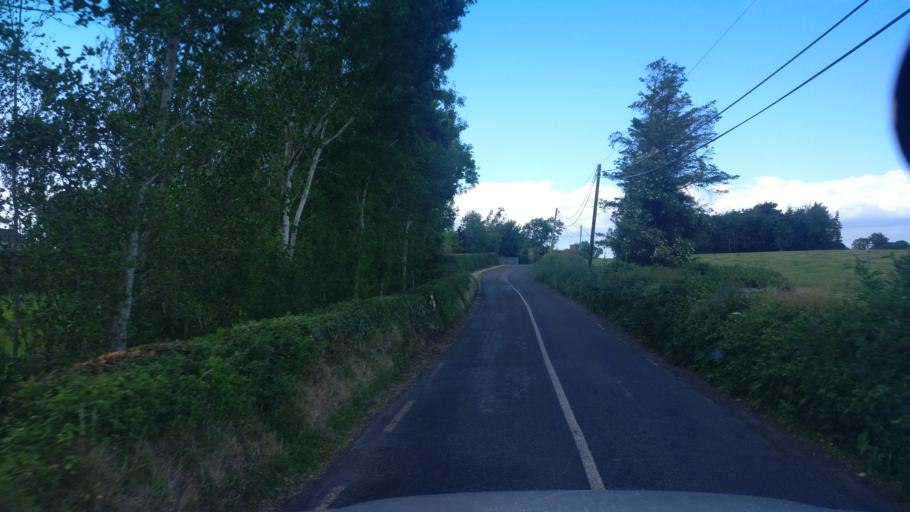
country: IE
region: Connaught
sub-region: County Galway
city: Portumna
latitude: 53.1831
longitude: -8.2992
